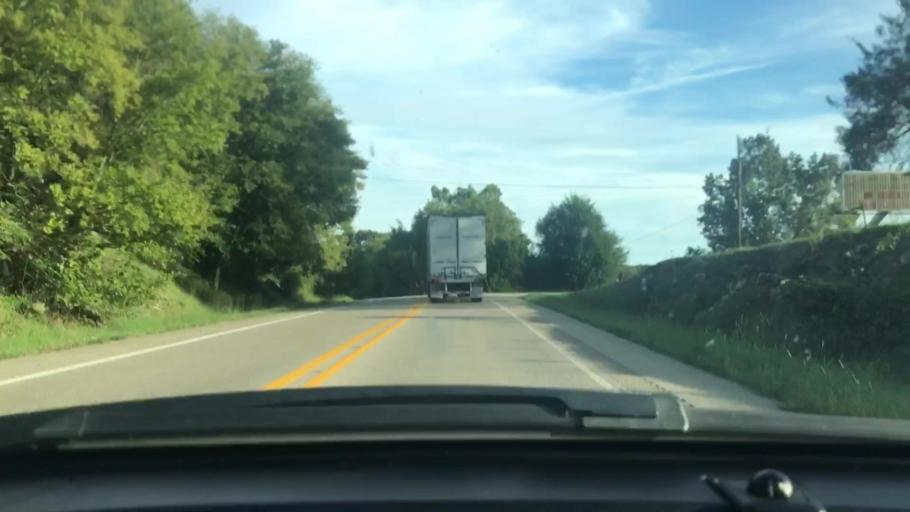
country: US
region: Arkansas
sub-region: Randolph County
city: Pocahontas
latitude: 36.2148
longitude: -91.2148
